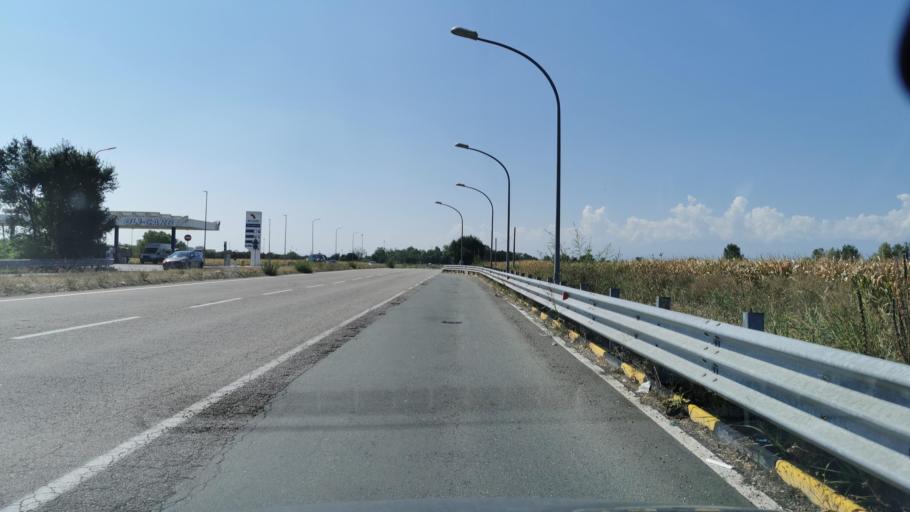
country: IT
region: Piedmont
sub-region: Provincia di Torino
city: Grugliasco
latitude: 45.0476
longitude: 7.5638
